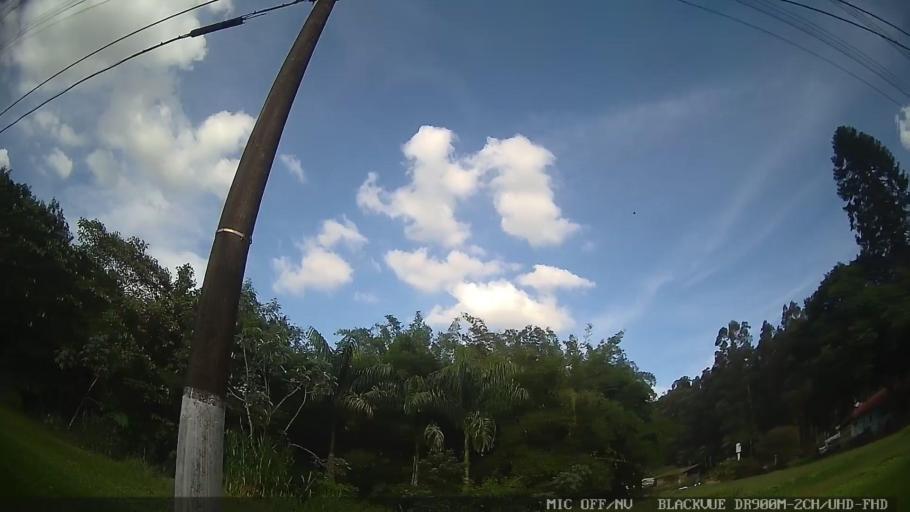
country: BR
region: Sao Paulo
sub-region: Jaguariuna
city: Jaguariuna
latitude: -22.6378
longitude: -47.0606
